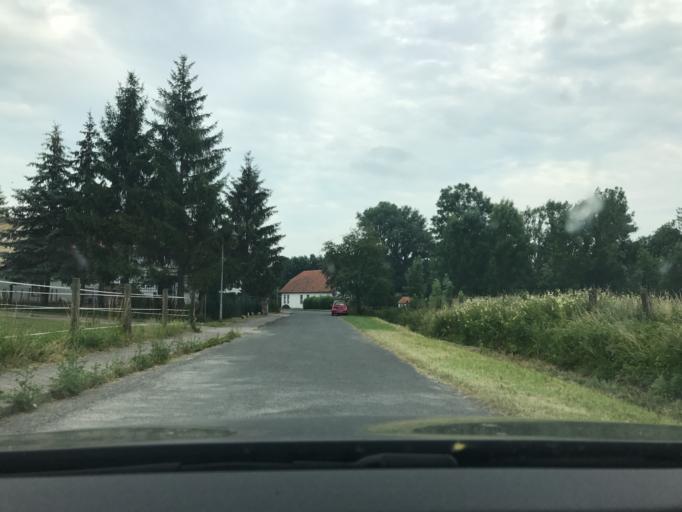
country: DE
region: Thuringia
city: Anrode
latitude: 51.2549
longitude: 10.3858
